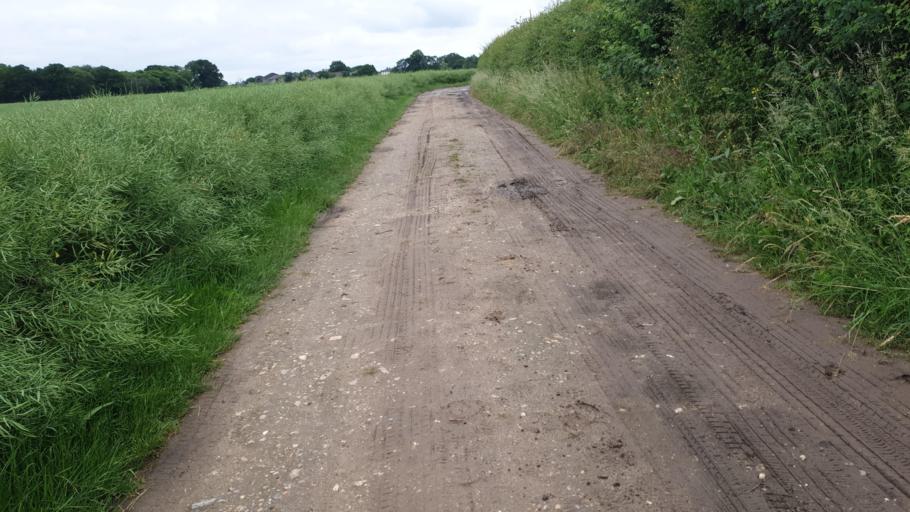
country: GB
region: England
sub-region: Essex
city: Great Bentley
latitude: 51.8831
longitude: 1.0632
